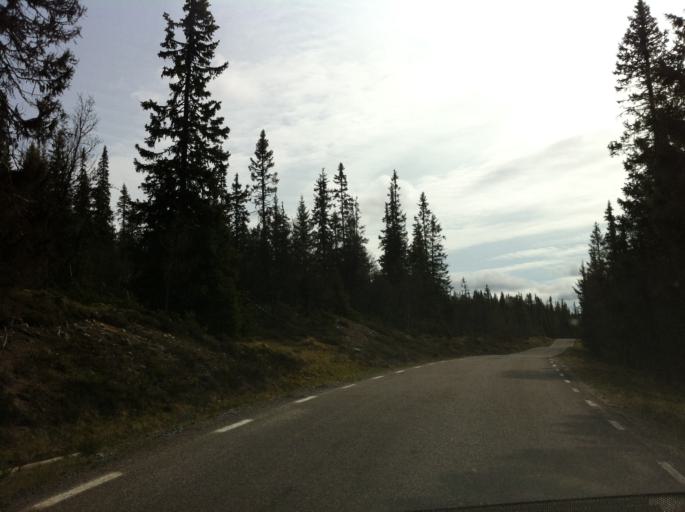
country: NO
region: Hedmark
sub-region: Engerdal
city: Engerdal
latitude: 62.3016
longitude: 12.8016
